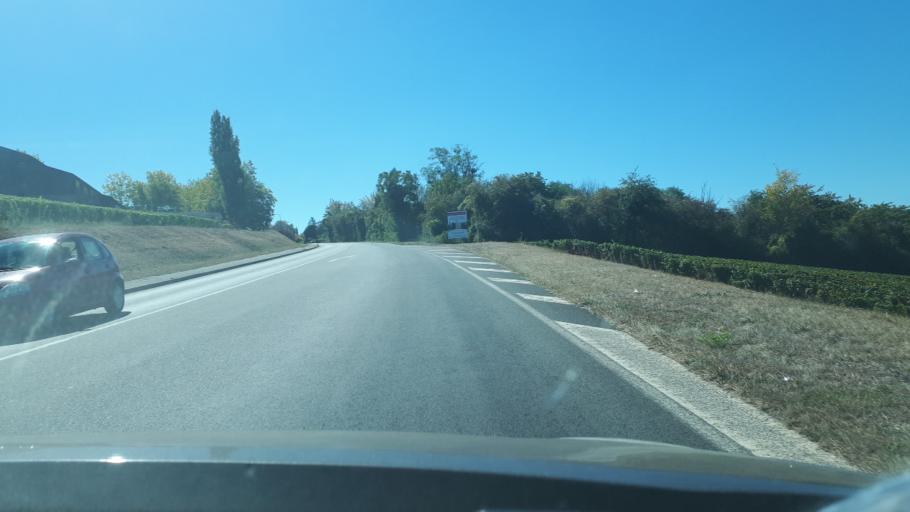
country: FR
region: Centre
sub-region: Departement du Cher
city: Sancerre
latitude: 47.3344
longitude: 2.8328
